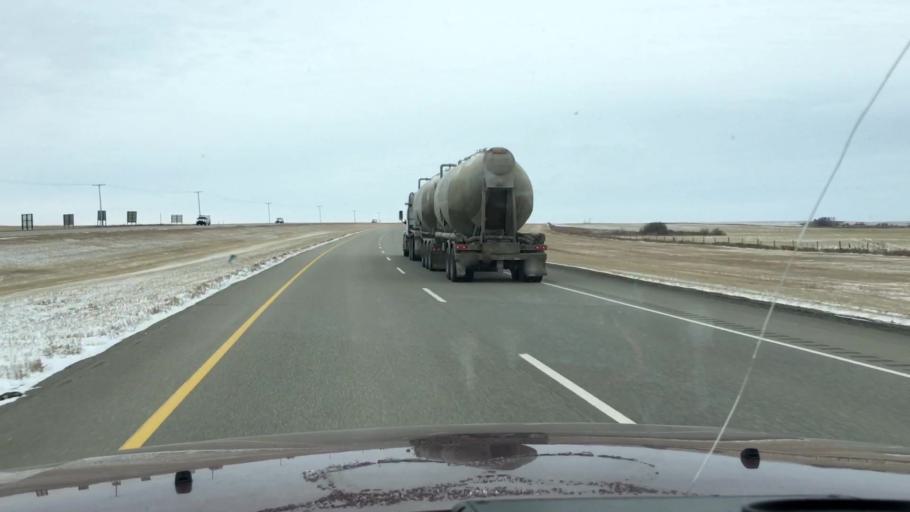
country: CA
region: Saskatchewan
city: Watrous
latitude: 51.2351
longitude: -105.9623
